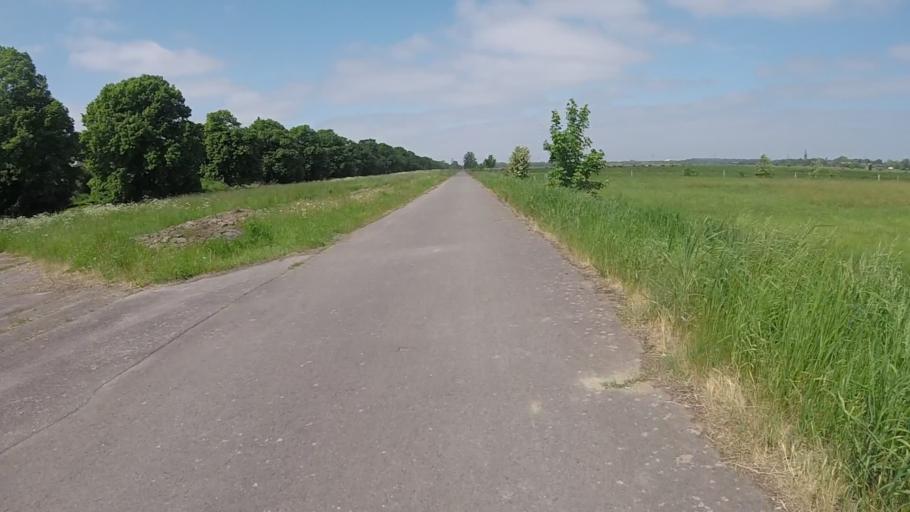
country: DE
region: Schleswig-Holstein
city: Oststeinbek
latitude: 53.5001
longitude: 10.1299
